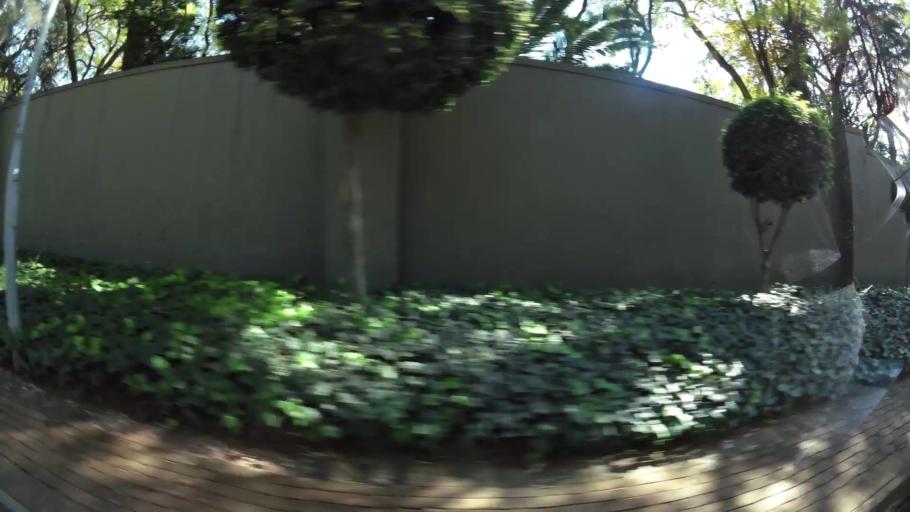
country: ZA
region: Gauteng
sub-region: City of Johannesburg Metropolitan Municipality
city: Johannesburg
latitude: -26.1121
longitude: 28.0402
